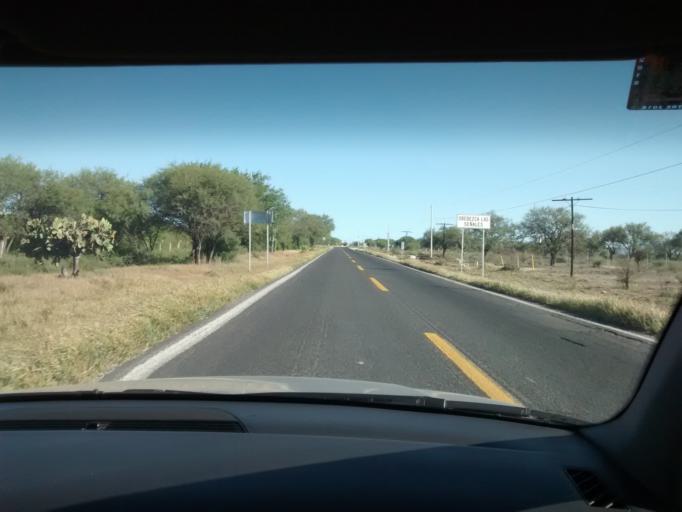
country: MX
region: Puebla
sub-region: Tepanco de Lopez
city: San Andres Cacaloapan
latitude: 18.5699
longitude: -97.5740
